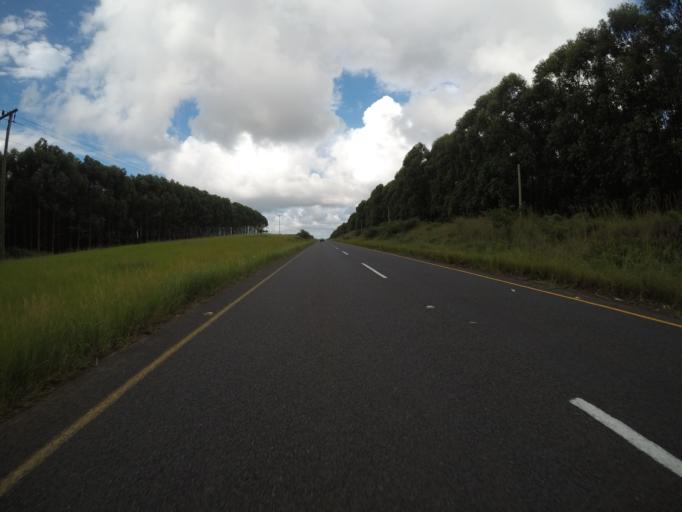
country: ZA
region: KwaZulu-Natal
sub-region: uMkhanyakude District Municipality
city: Mtubatuba
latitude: -28.3922
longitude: 32.2245
